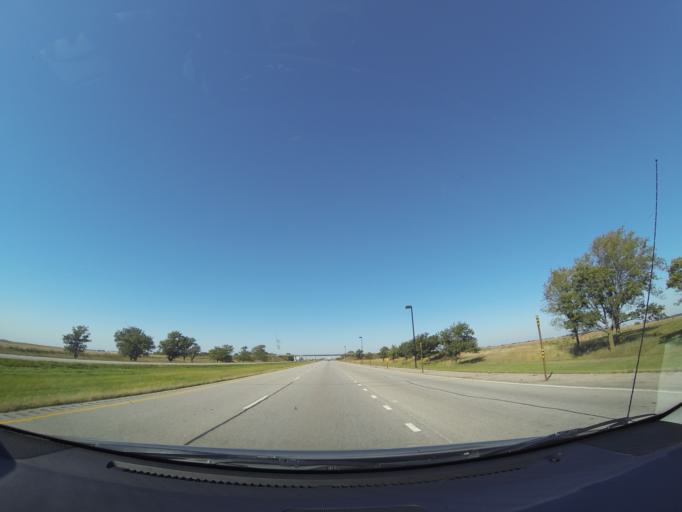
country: US
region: Nebraska
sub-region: Seward County
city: Seward
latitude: 40.8225
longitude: -97.1740
